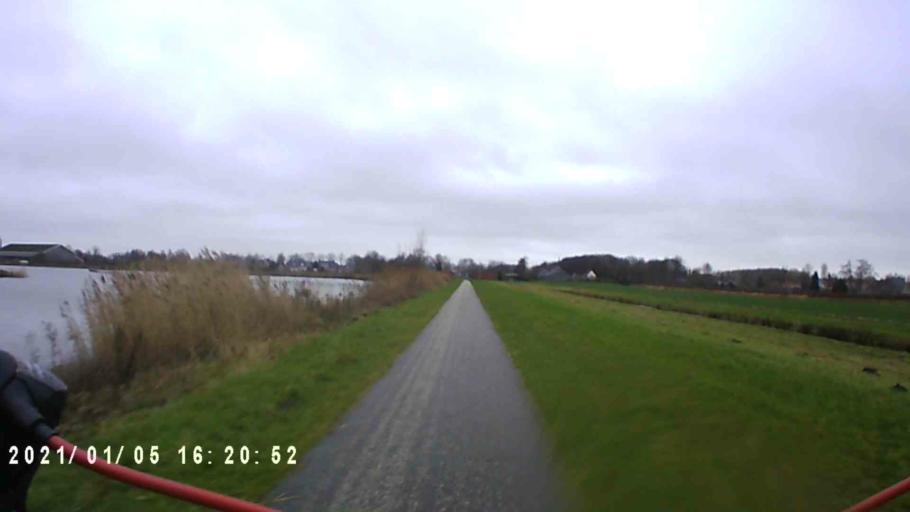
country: NL
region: Groningen
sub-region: Gemeente  Oldambt
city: Winschoten
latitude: 53.1982
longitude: 7.0436
